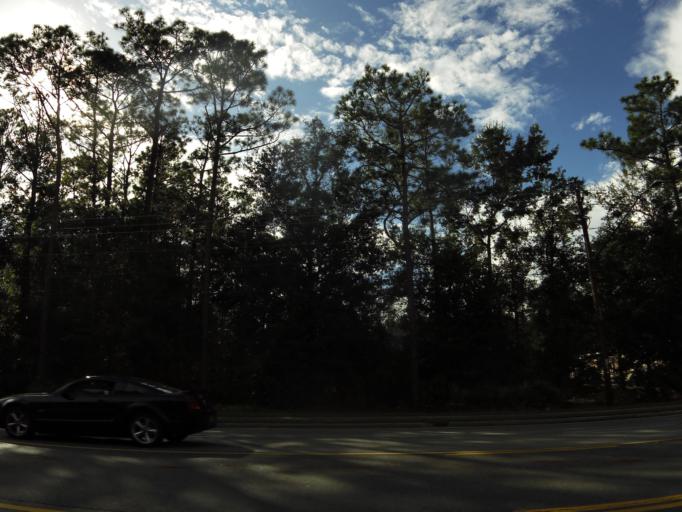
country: US
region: Georgia
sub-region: Liberty County
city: Hinesville
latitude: 31.8057
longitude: -81.6041
